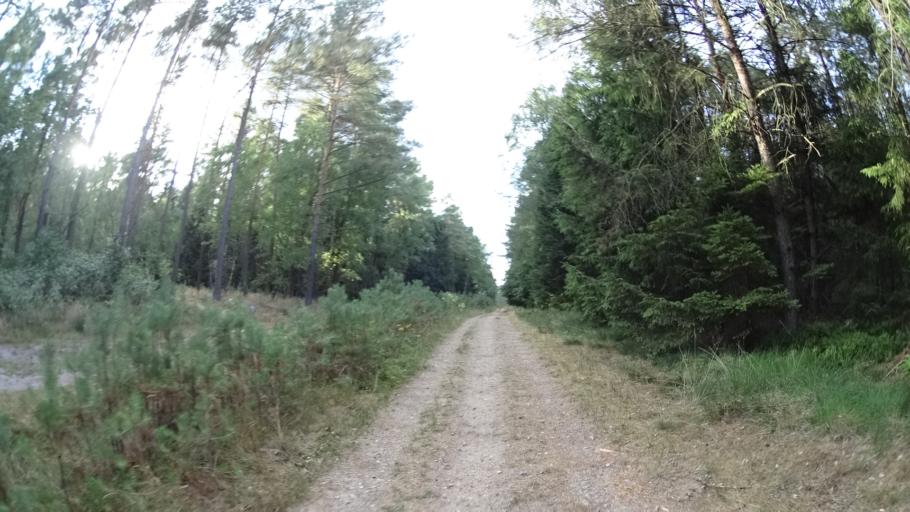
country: DE
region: Lower Saxony
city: Handeloh
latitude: 53.2259
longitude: 9.8746
